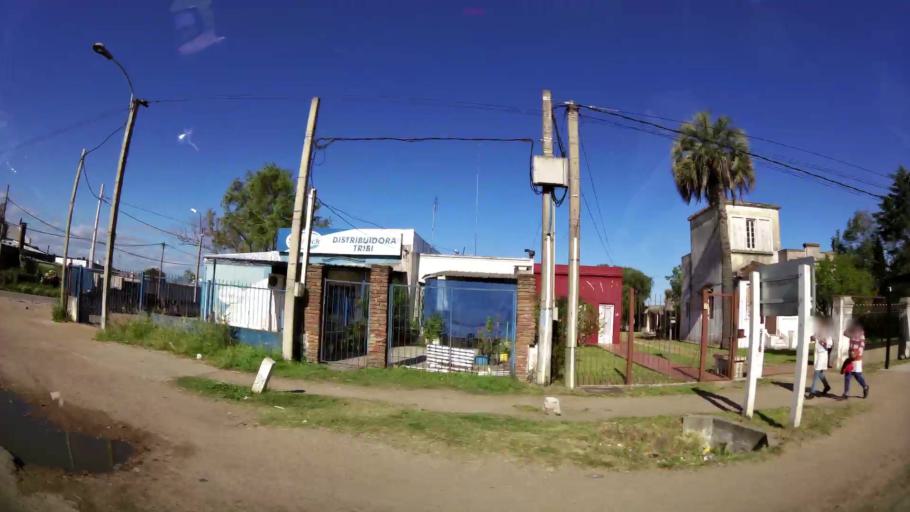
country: UY
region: Canelones
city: La Paz
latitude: -34.8085
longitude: -56.1605
